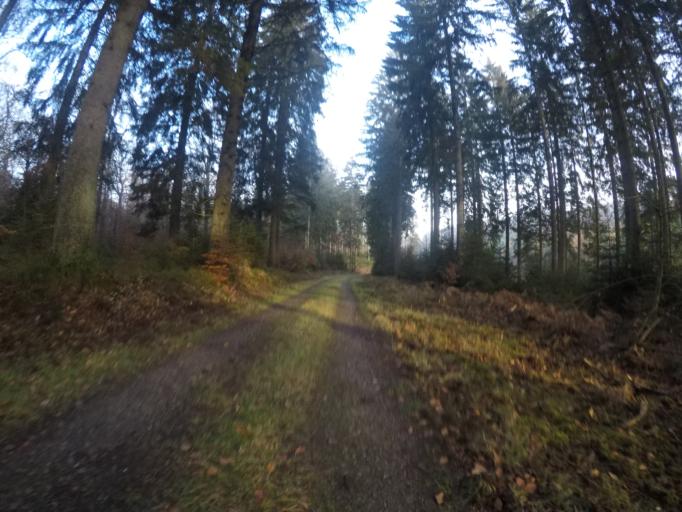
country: BE
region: Wallonia
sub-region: Province du Luxembourg
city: Habay-la-Vieille
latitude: 49.7585
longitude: 5.6598
